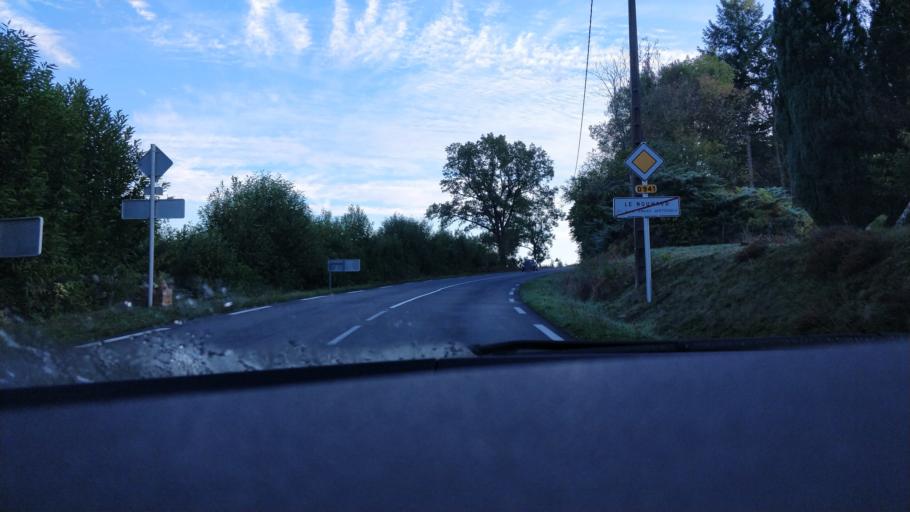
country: FR
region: Limousin
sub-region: Departement de la Haute-Vienne
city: Sauviat-sur-Vige
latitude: 45.9211
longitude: 1.6403
